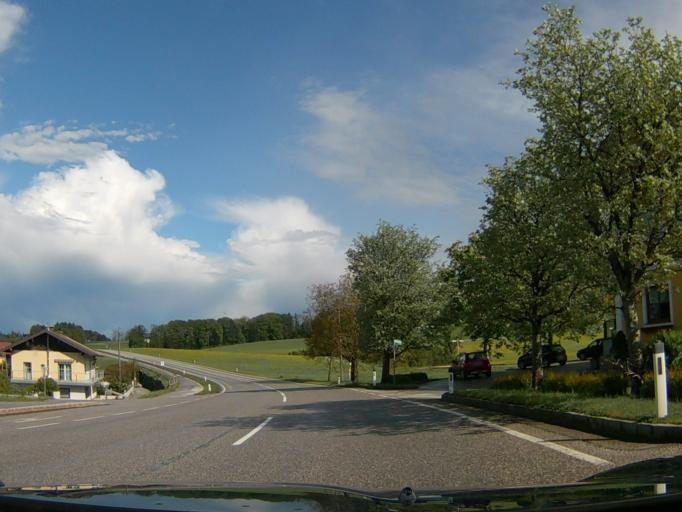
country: AT
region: Salzburg
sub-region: Politischer Bezirk Salzburg-Umgebung
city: Plainfeld
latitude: 47.8554
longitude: 13.1784
